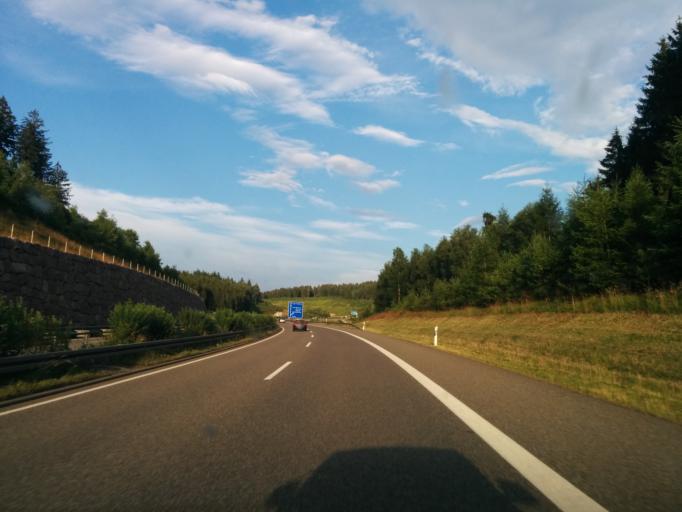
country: DE
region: Thuringia
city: Bischofrod
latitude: 50.5889
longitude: 10.6563
